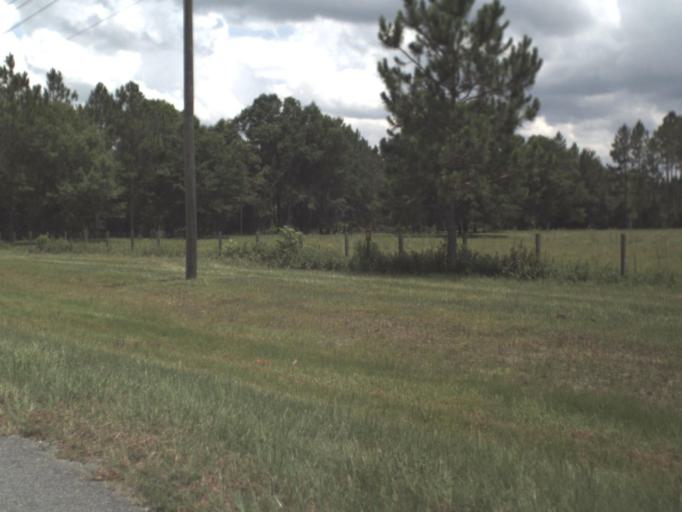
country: US
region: Florida
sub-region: Union County
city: Lake Butler
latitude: 30.0433
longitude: -82.2836
